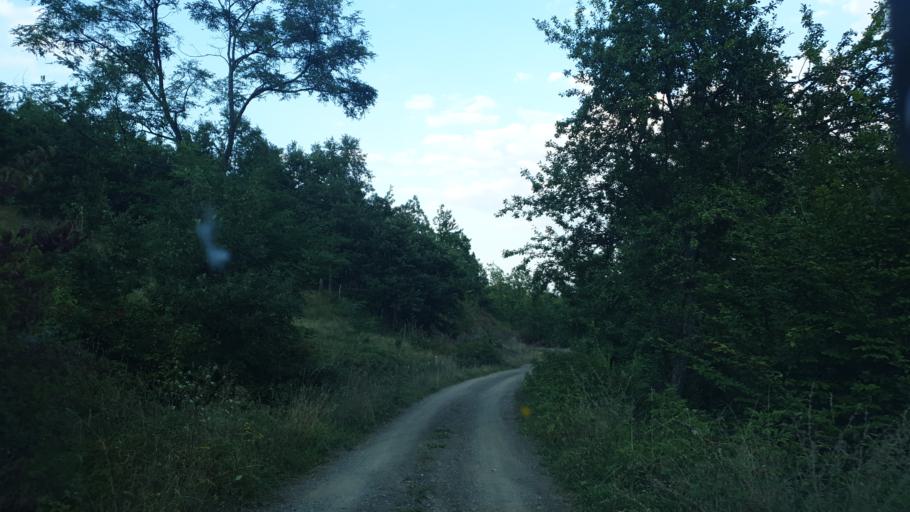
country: RS
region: Central Serbia
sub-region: Zlatiborski Okrug
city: Kosjeric
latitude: 44.0096
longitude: 19.9926
